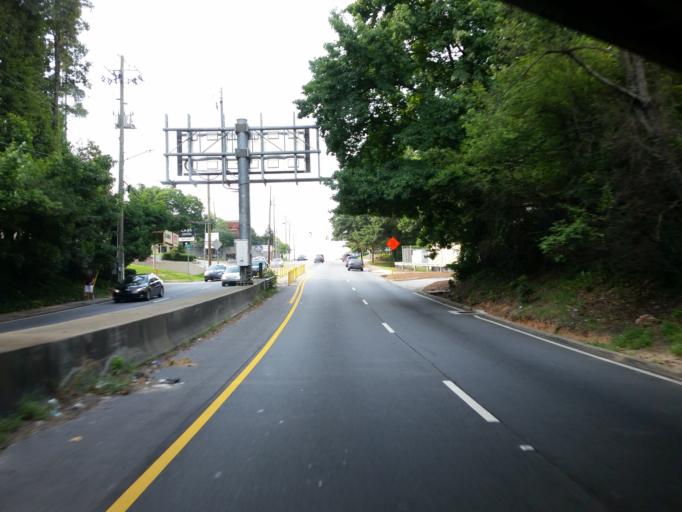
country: US
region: Georgia
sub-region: Fulton County
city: Atlanta
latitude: 33.7988
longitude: -84.4078
